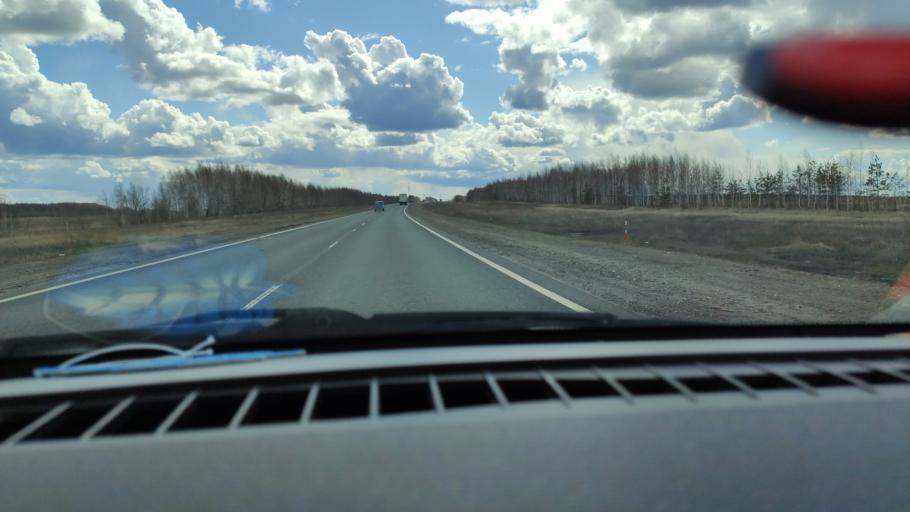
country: RU
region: Saratov
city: Dukhovnitskoye
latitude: 52.8453
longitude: 48.2519
